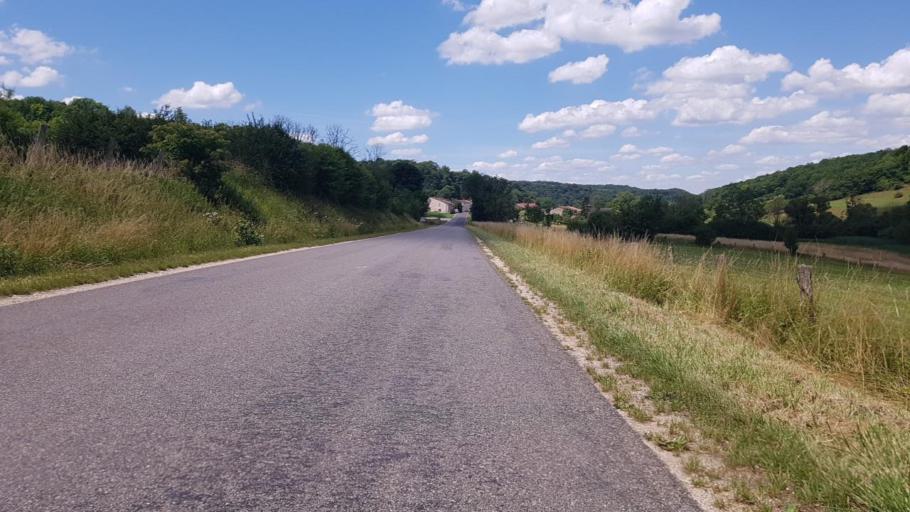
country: FR
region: Lorraine
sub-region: Departement de la Meuse
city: Gondrecourt-le-Chateau
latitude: 48.6298
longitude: 5.4743
